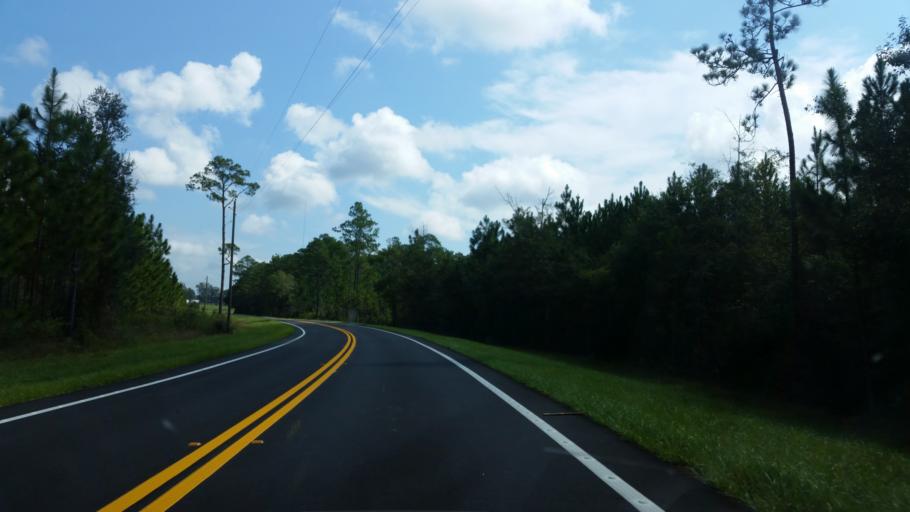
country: US
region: Florida
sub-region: Escambia County
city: Molino
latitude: 30.6945
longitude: -87.4312
